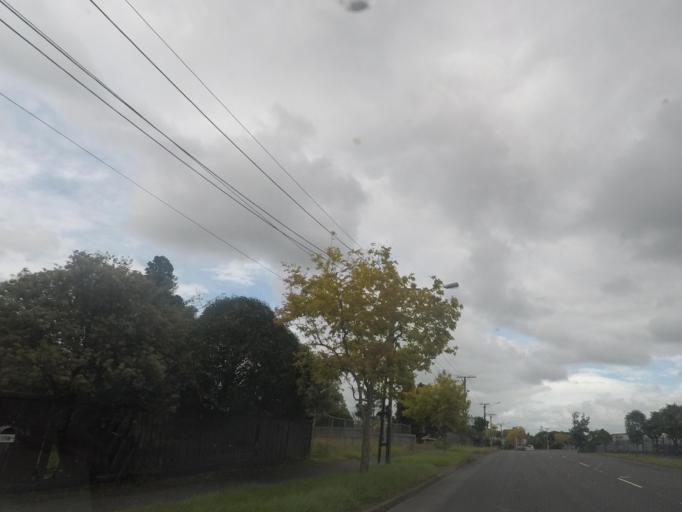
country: NZ
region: Auckland
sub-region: Auckland
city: Tamaki
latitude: -36.8778
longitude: 174.8689
